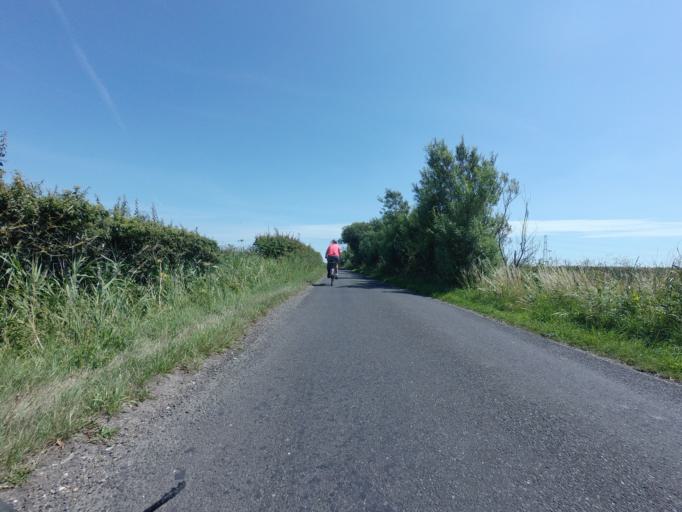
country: GB
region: England
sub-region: Kent
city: Lydd
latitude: 50.9786
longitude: 0.8952
